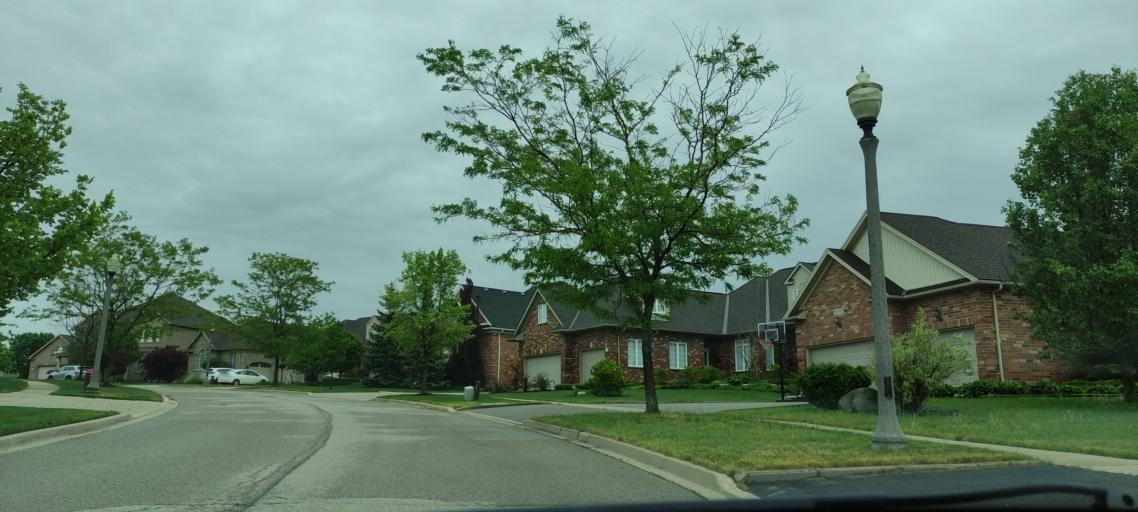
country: CA
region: Ontario
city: Kitchener
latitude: 43.4006
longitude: -80.5446
